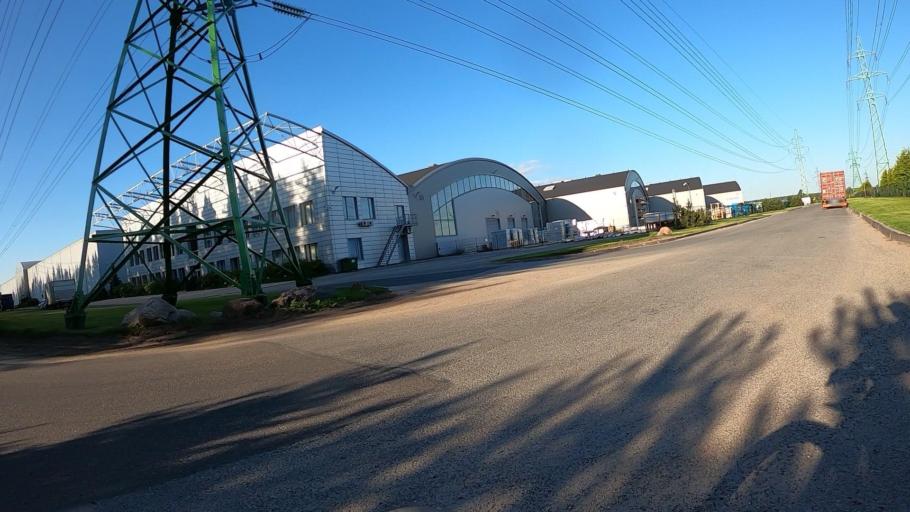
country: LV
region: Stopini
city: Ulbroka
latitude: 56.9300
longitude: 24.2357
